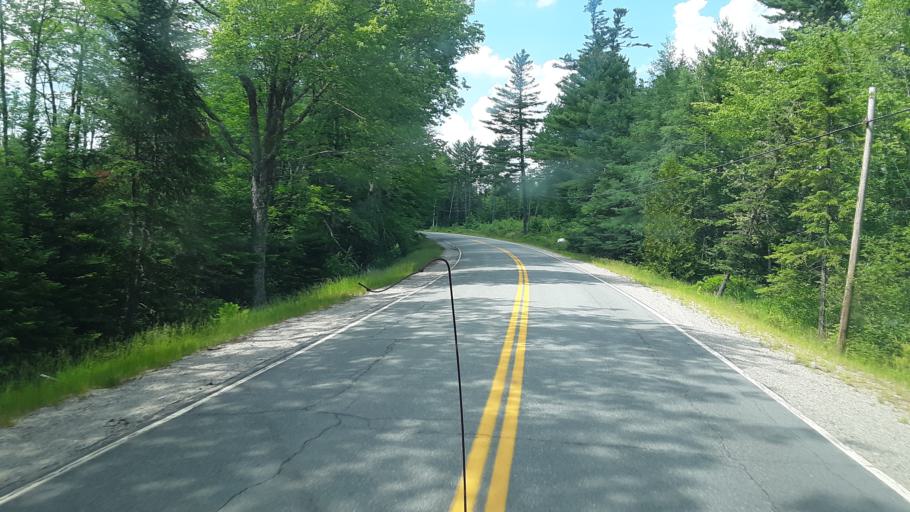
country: US
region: Maine
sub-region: Washington County
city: Machias
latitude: 44.8933
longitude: -67.6238
